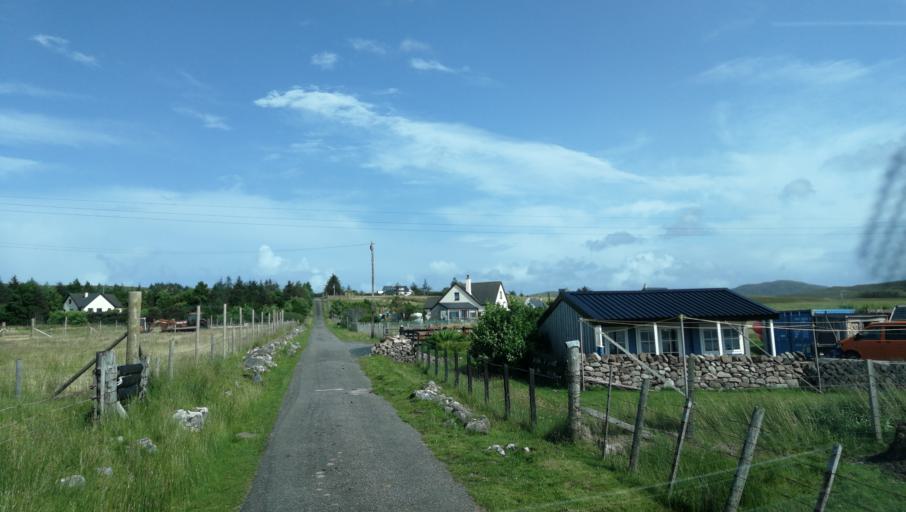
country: GB
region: Scotland
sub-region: Highland
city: Portree
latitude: 57.7426
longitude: -5.7774
